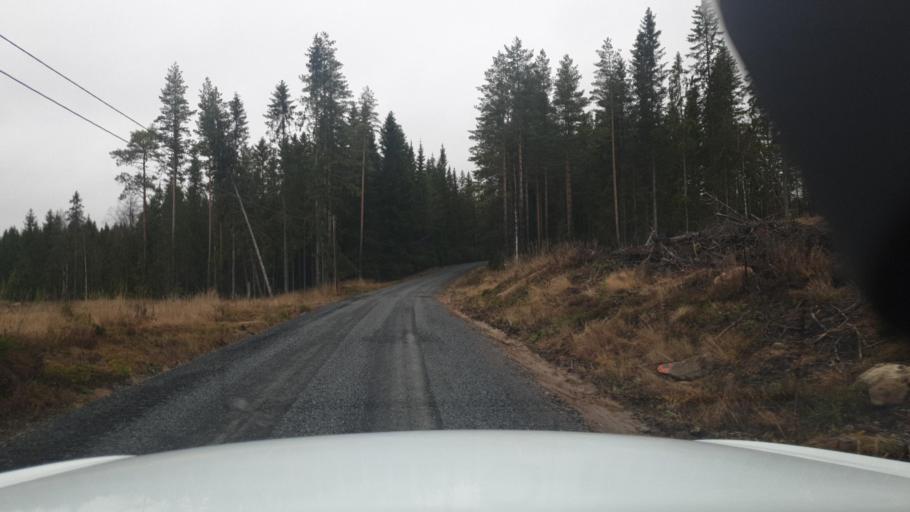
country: SE
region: Vaermland
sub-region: Eda Kommun
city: Charlottenberg
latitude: 60.1475
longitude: 12.5956
